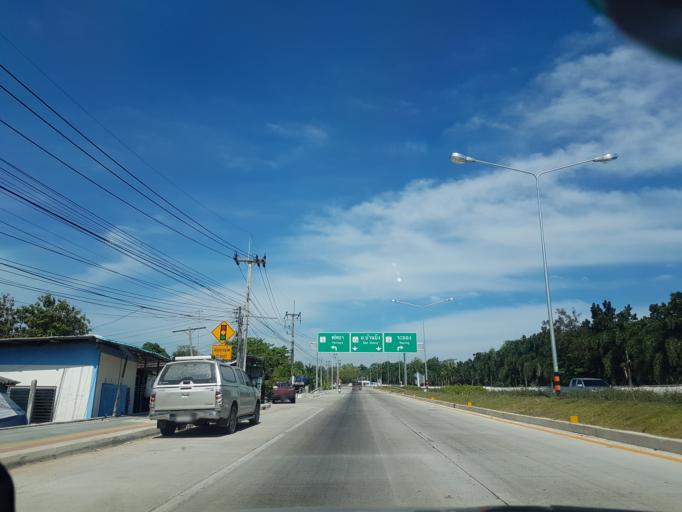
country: TH
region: Chon Buri
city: Sattahip
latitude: 12.6859
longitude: 100.9787
